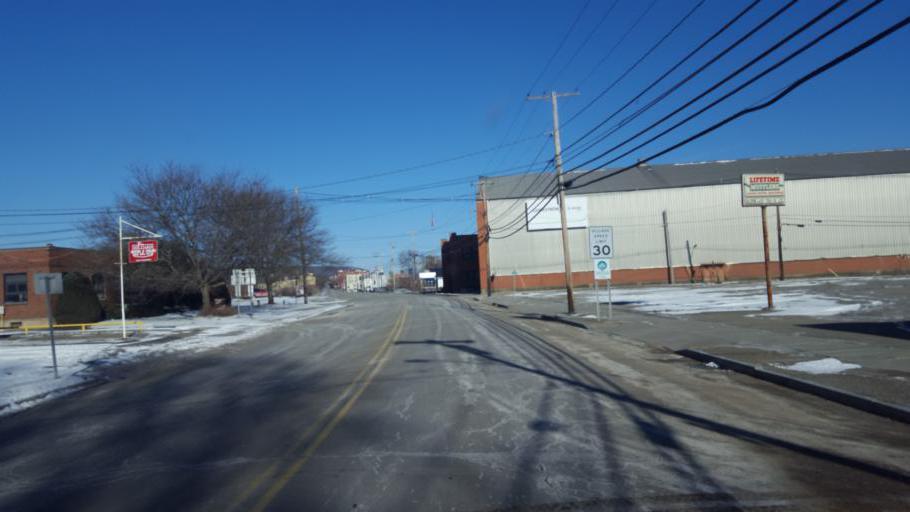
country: US
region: New York
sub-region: Allegany County
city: Wellsville
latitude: 42.1167
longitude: -77.9396
